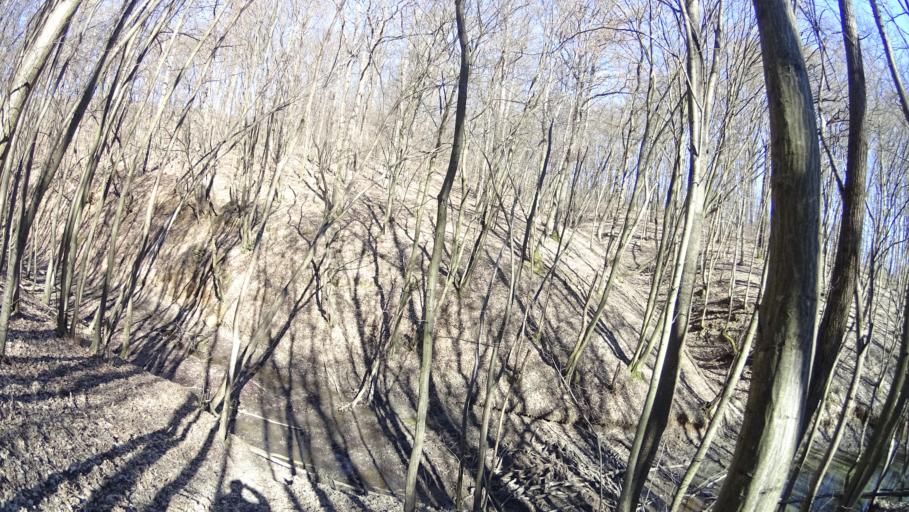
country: HU
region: Pest
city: Veroce
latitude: 47.8615
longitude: 19.0875
